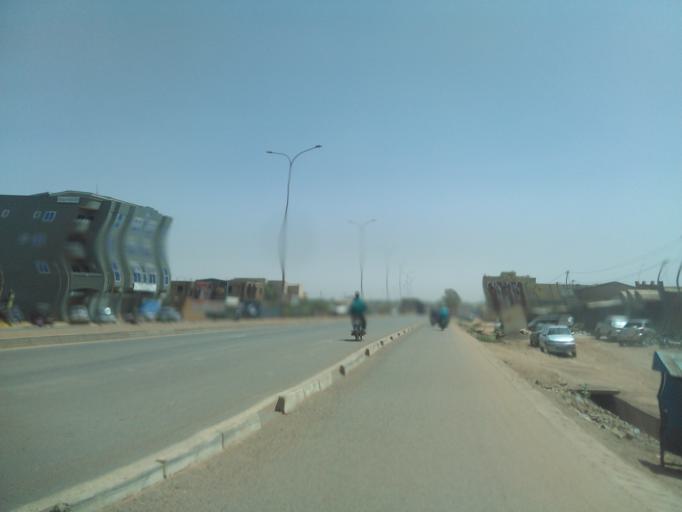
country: BF
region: Centre
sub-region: Kadiogo Province
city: Ouagadougou
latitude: 12.3369
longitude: -1.5456
